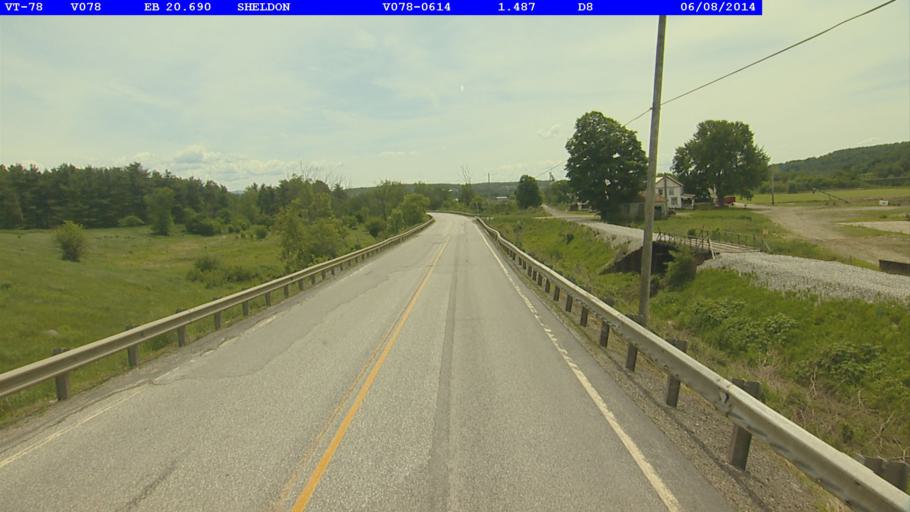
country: US
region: Vermont
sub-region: Franklin County
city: Enosburg Falls
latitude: 44.9071
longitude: -72.9512
